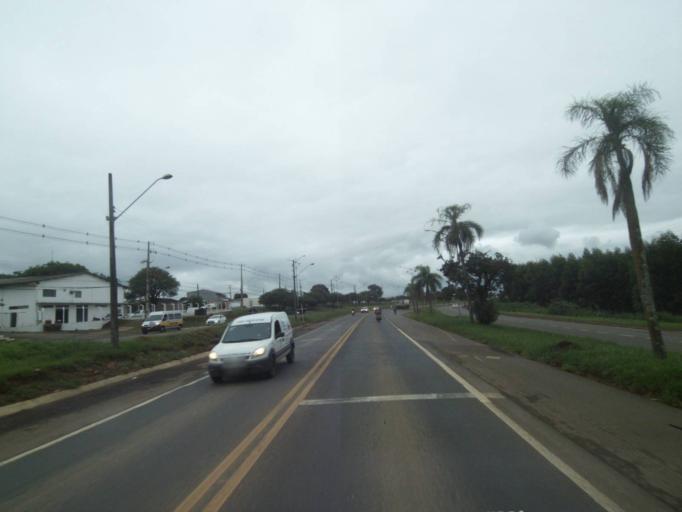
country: BR
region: Parana
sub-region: Telemaco Borba
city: Telemaco Borba
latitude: -24.3367
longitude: -50.6560
